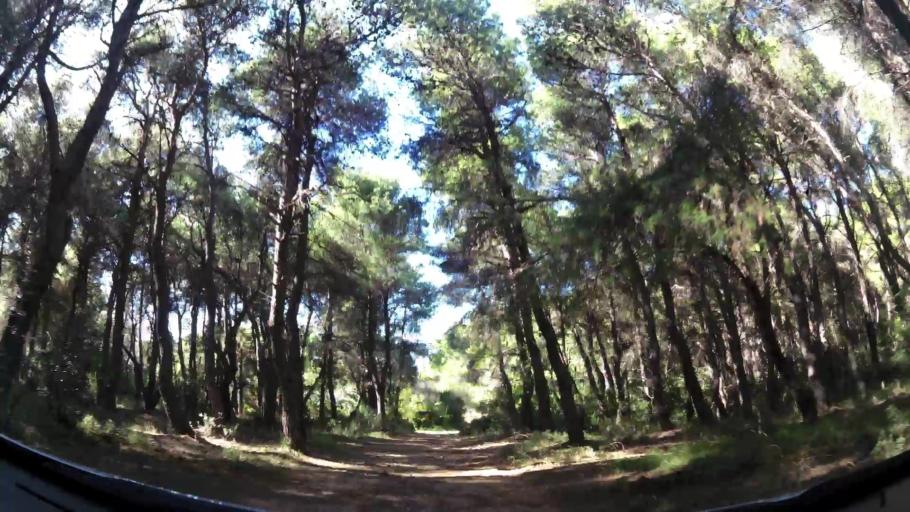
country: GR
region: Attica
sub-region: Nomarchia Athinas
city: Ekali
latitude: 38.1100
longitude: 23.8289
